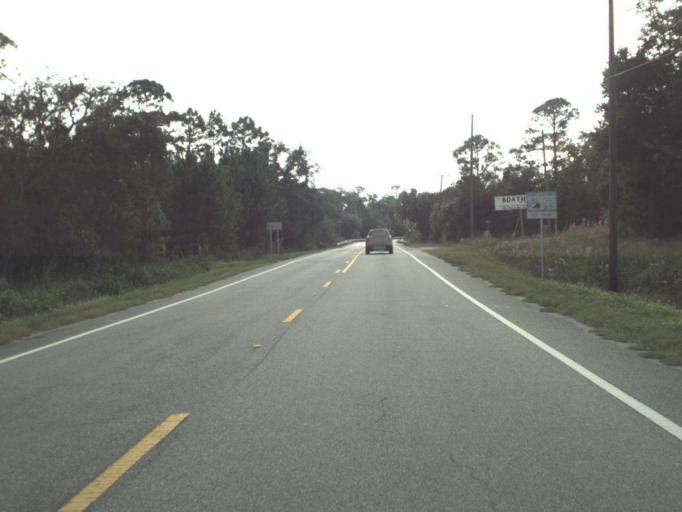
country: US
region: Florida
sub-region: Franklin County
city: Carrabelle
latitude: 29.8366
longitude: -84.6825
